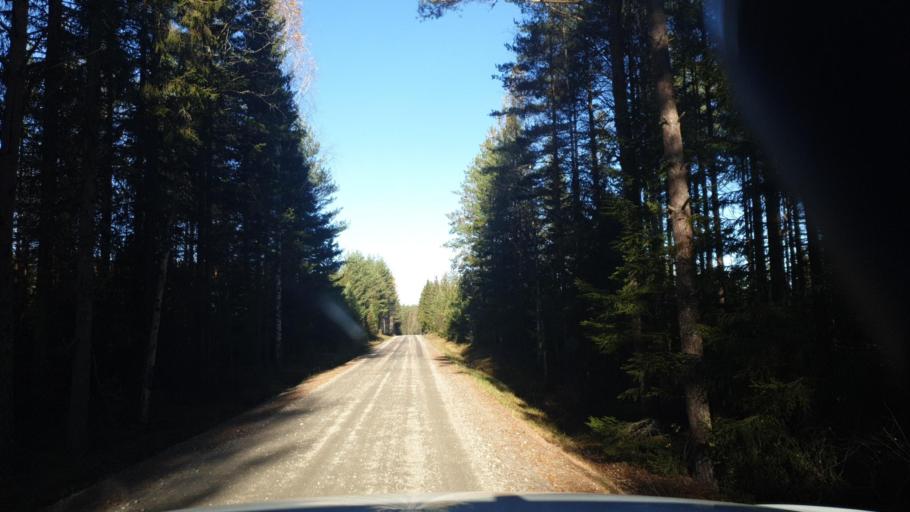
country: SE
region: Vaermland
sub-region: Karlstads Kommun
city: Edsvalla
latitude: 59.5251
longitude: 13.0012
